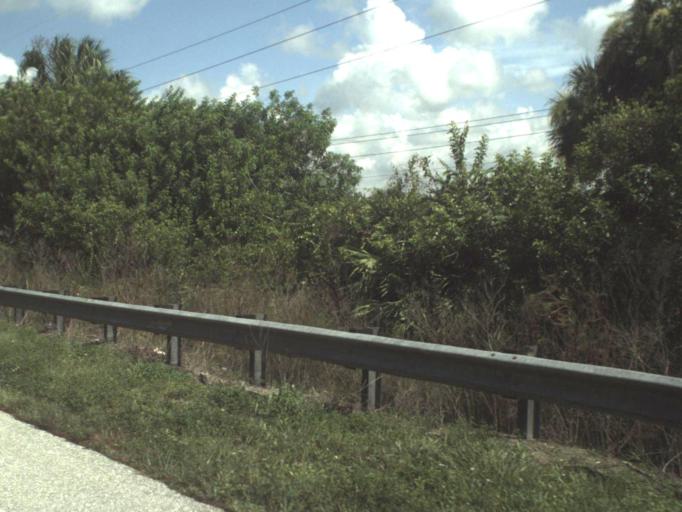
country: US
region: Florida
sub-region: Martin County
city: Indiantown
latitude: 27.0973
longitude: -80.5841
